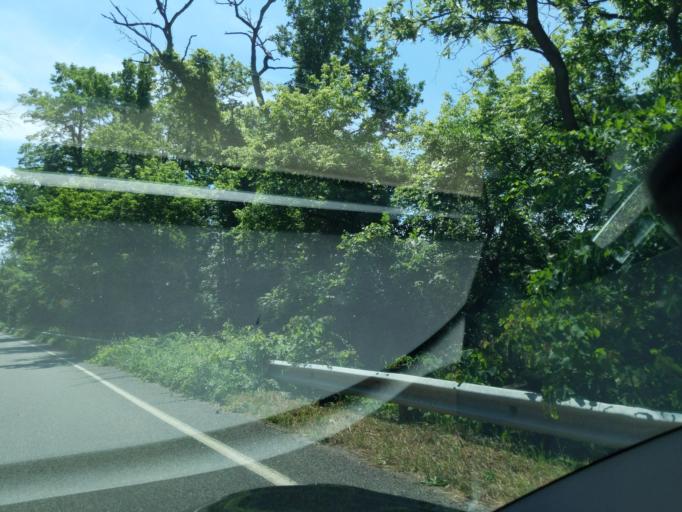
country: US
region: Michigan
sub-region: Kent County
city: Forest Hills
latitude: 42.9603
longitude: -85.4808
